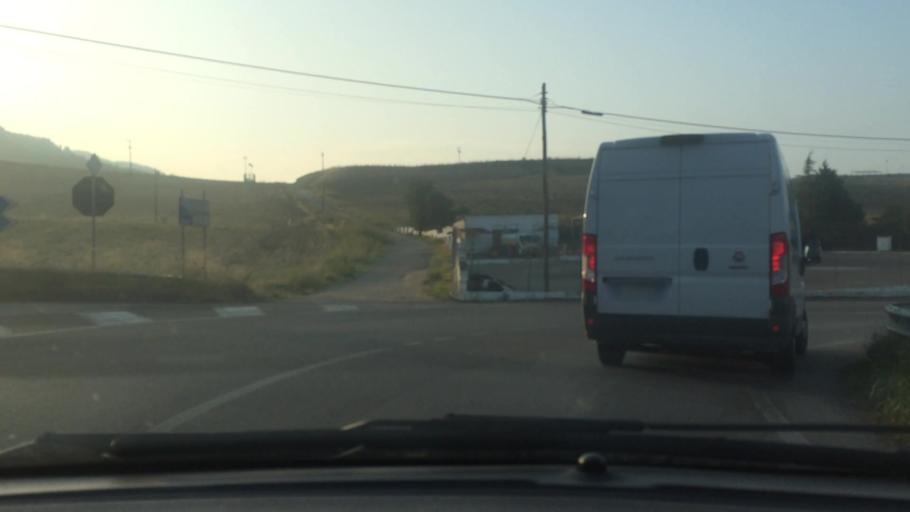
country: IT
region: Basilicate
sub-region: Provincia di Matera
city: Montescaglioso
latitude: 40.5351
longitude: 16.6457
